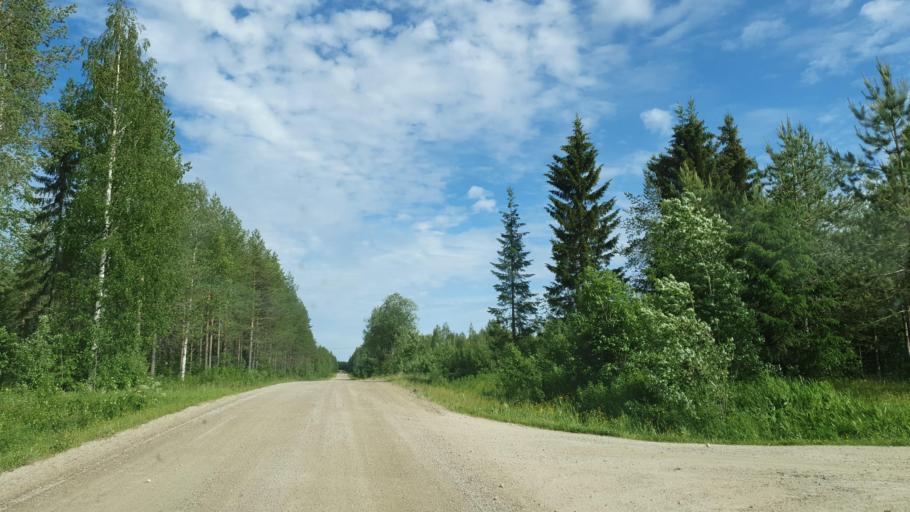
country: FI
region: Kainuu
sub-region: Kehys-Kainuu
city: Kuhmo
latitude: 64.5151
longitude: 29.4071
